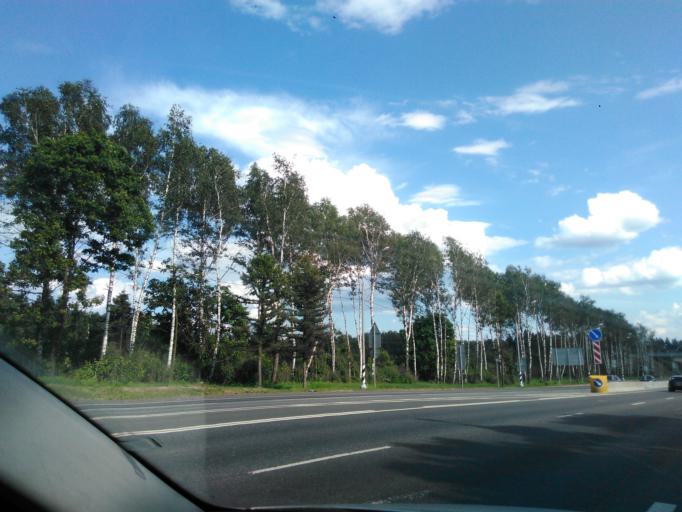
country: RU
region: Moskovskaya
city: Peshki
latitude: 56.1528
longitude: 37.0325
